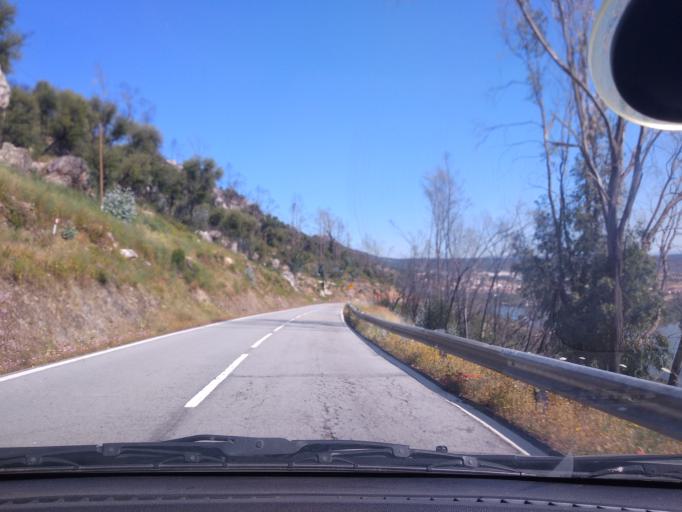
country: PT
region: Portalegre
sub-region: Nisa
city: Nisa
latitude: 39.6341
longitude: -7.6655
